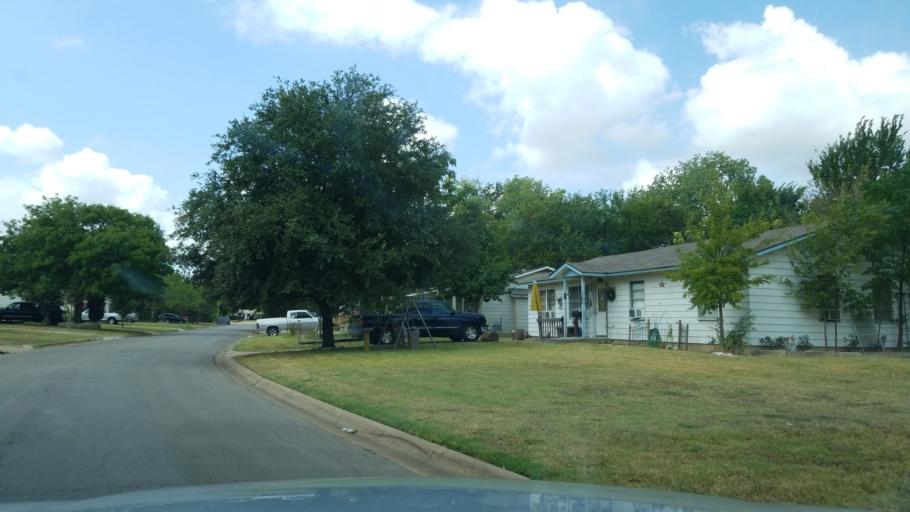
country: US
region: Texas
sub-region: Tarrant County
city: Euless
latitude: 32.8465
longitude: -97.0849
